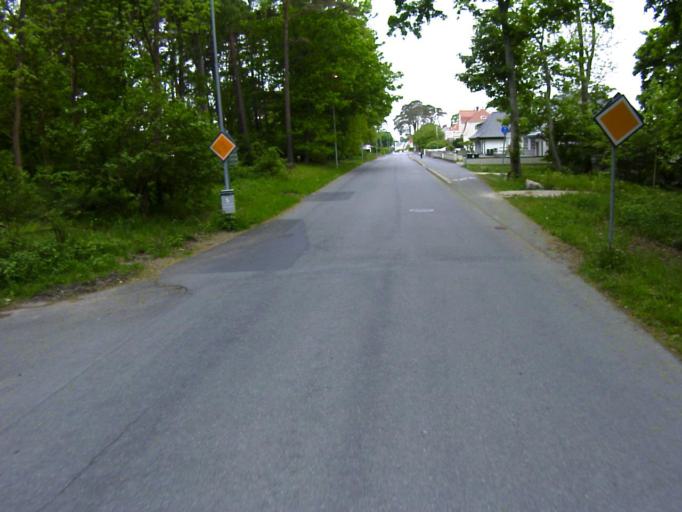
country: SE
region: Skane
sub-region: Kristianstads Kommun
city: Ahus
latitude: 55.9229
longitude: 14.3011
